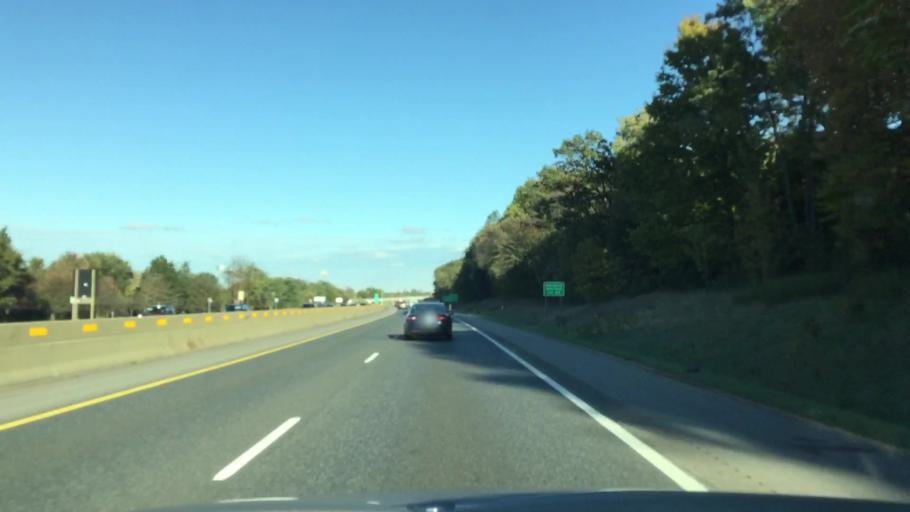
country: US
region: Michigan
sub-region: Kalamazoo County
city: Galesburg
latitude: 42.2709
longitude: -85.4394
